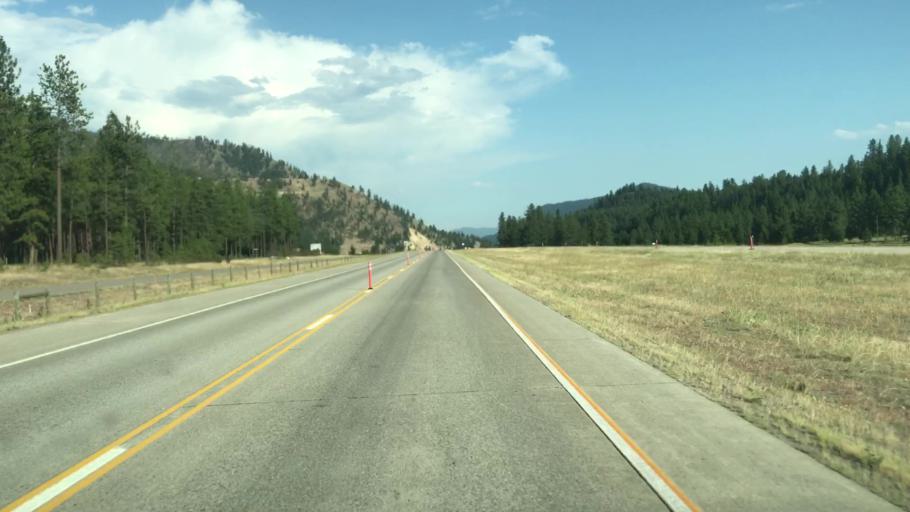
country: US
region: Montana
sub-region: Mineral County
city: Superior
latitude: 47.2321
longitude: -114.9826
